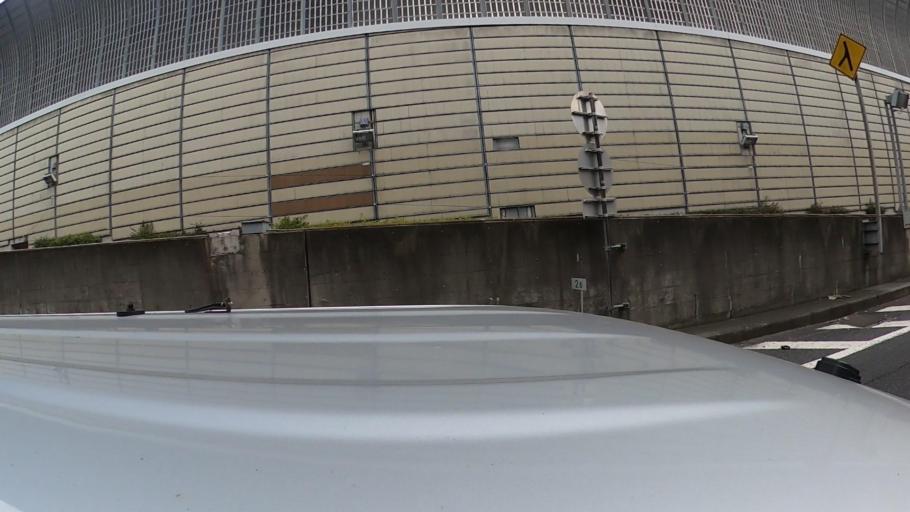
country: JP
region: Saitama
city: Wako
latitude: 35.7803
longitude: 139.6097
